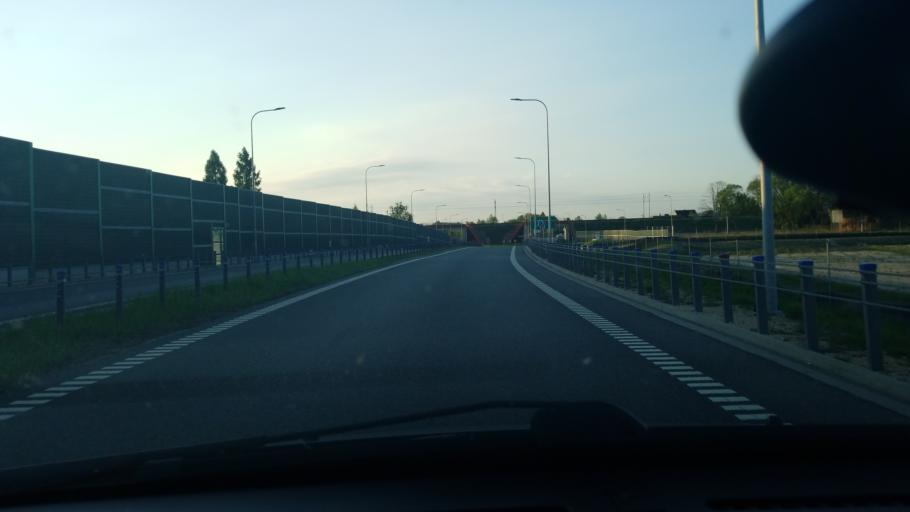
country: PL
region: Silesian Voivodeship
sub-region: Powiat czestochowski
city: Blachownia
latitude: 50.7827
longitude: 19.0105
